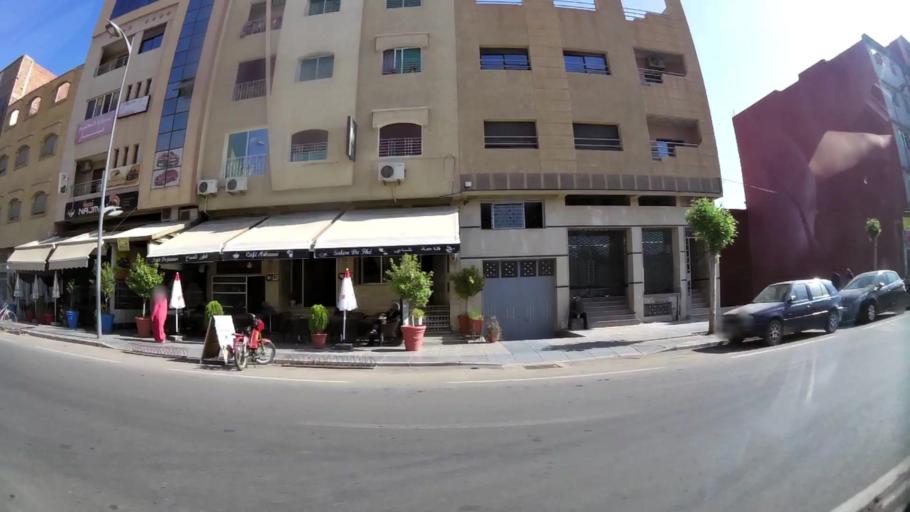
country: MA
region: Oriental
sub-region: Oujda-Angad
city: Oujda
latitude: 34.6819
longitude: -1.9419
